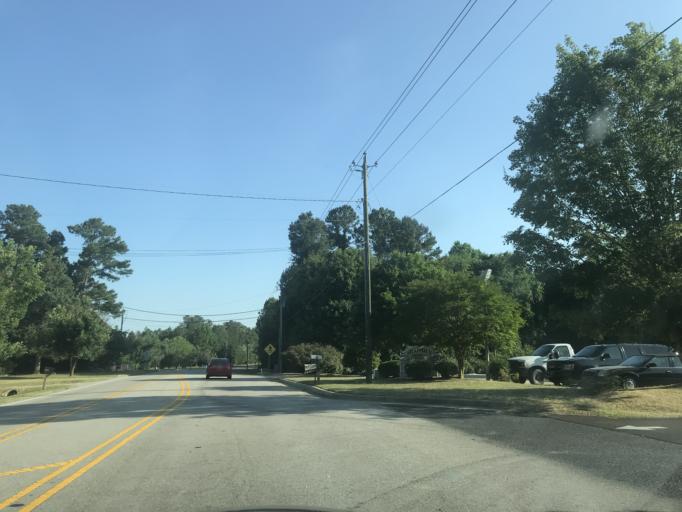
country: US
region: North Carolina
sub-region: Wake County
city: Garner
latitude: 35.7165
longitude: -78.6024
